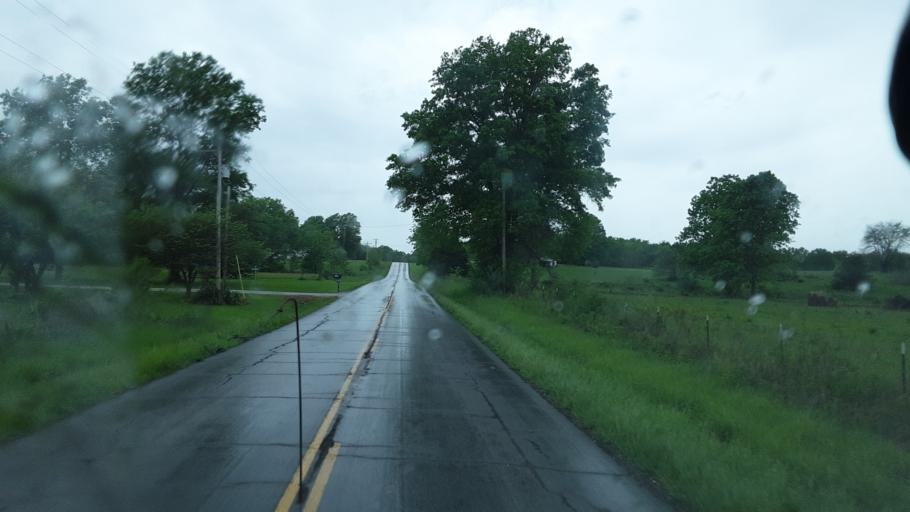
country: US
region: Missouri
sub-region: Boone County
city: Centralia
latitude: 39.3886
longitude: -92.2260
